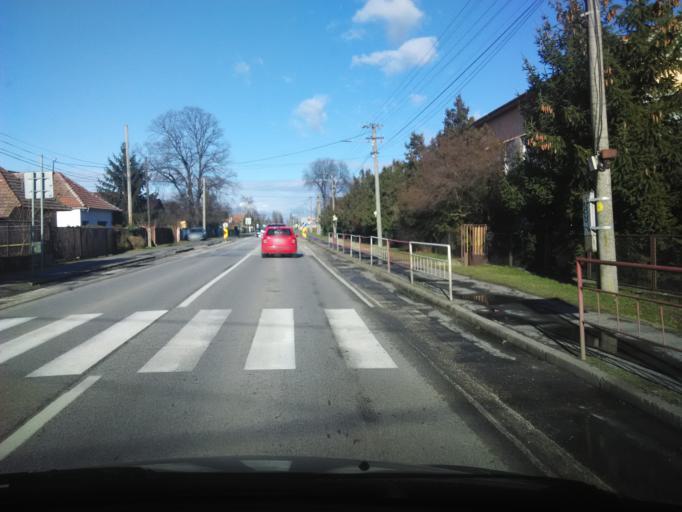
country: SK
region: Nitriansky
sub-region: Okres Nitra
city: Nitra
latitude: 48.2170
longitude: 18.1438
